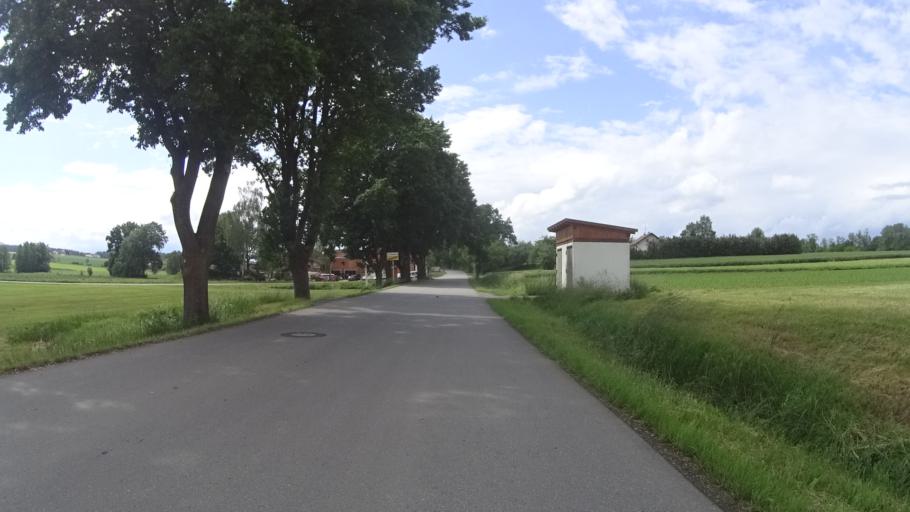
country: DE
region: Bavaria
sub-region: Lower Bavaria
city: Gangkofen
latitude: 48.4421
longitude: 12.5454
